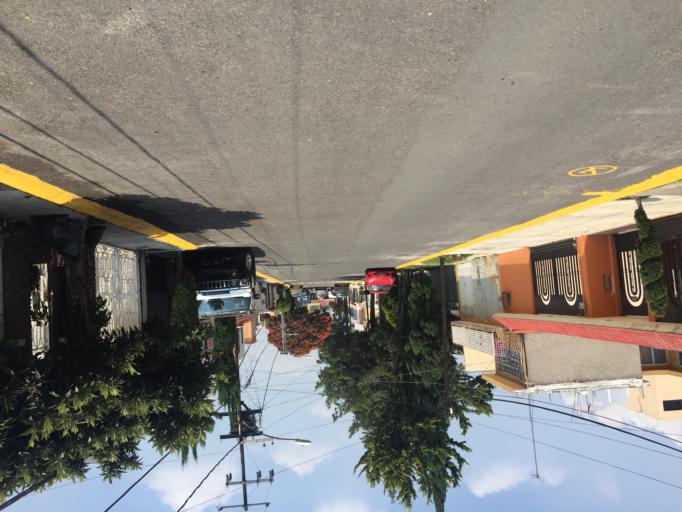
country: MX
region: Mexico
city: Cuautitlan Izcalli
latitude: 19.6507
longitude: -99.2126
